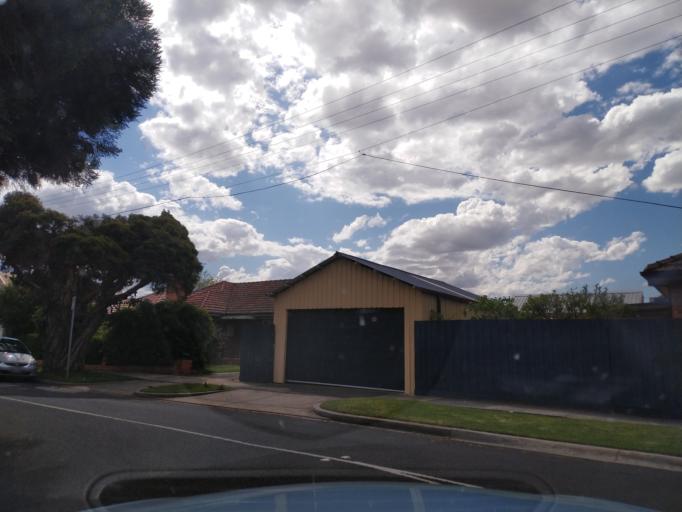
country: AU
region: Victoria
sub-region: Hobsons Bay
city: Newport
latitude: -37.8468
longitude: 144.8795
